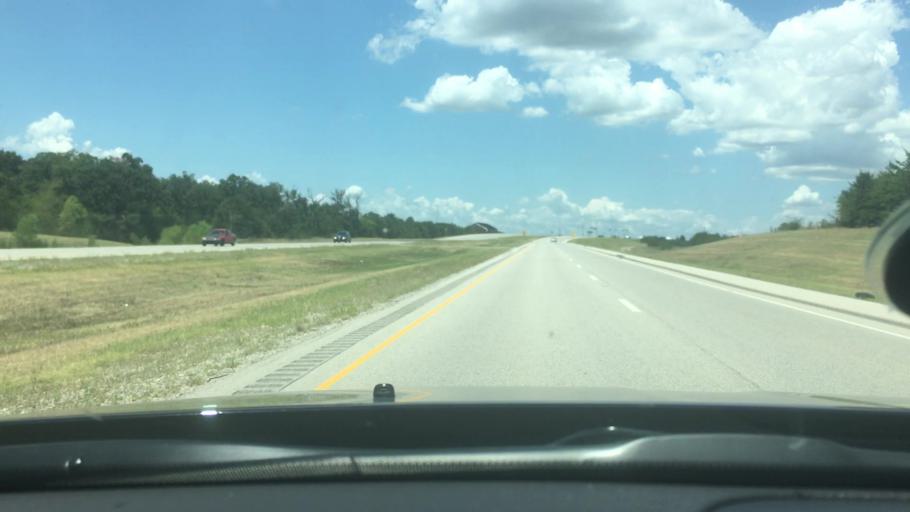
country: US
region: Oklahoma
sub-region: Bryan County
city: Durant
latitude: 33.9920
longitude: -96.4278
